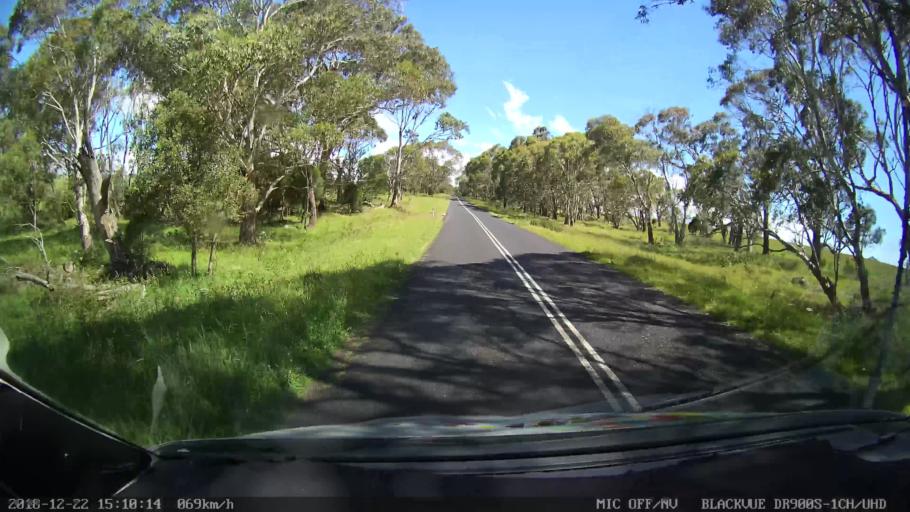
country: AU
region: New South Wales
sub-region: Bellingen
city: Dorrigo
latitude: -30.3327
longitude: 152.4053
